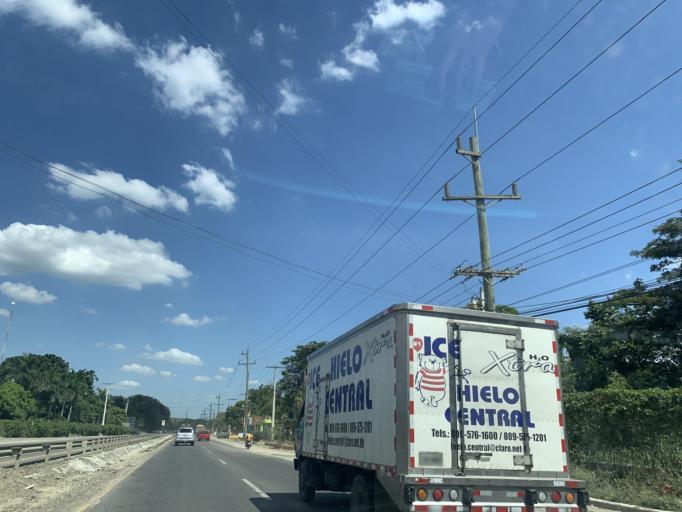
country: DO
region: Santiago
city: Villa Bisono
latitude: 19.5516
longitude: -70.8570
